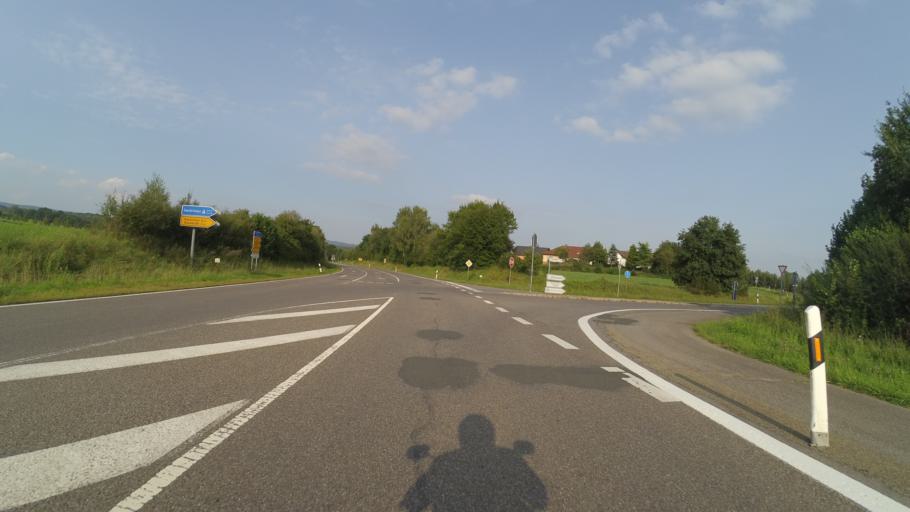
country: DE
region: Saarland
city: Wadern
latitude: 49.5403
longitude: 6.8754
